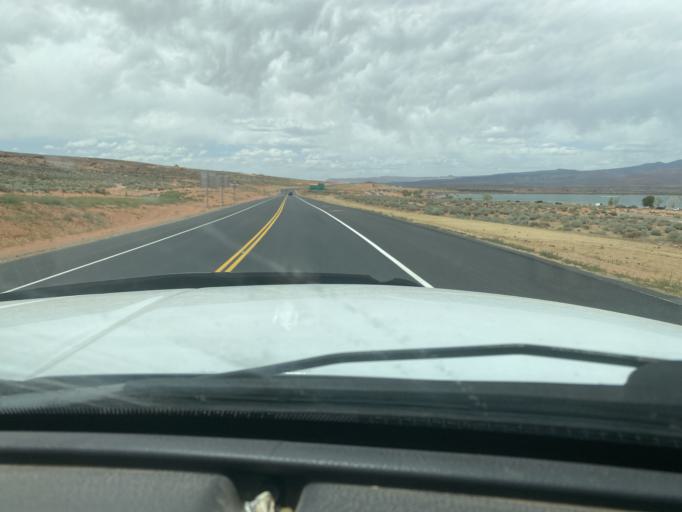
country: US
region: Utah
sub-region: Washington County
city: Hurricane
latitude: 37.1015
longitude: -113.3825
